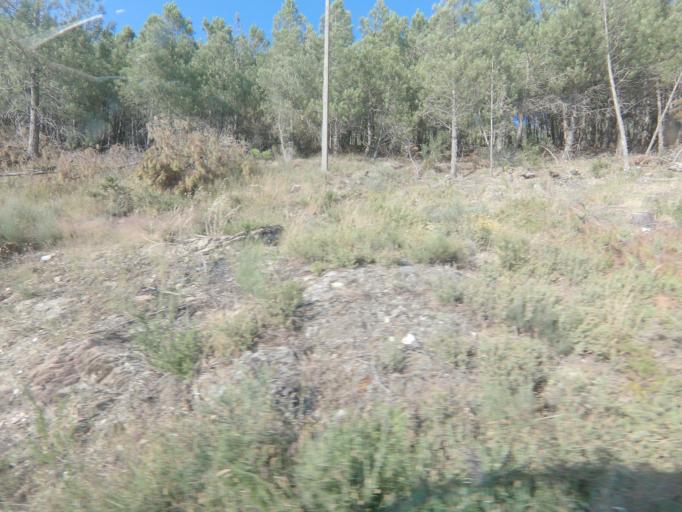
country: PT
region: Vila Real
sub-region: Sabrosa
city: Vilela
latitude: 41.1920
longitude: -7.6190
